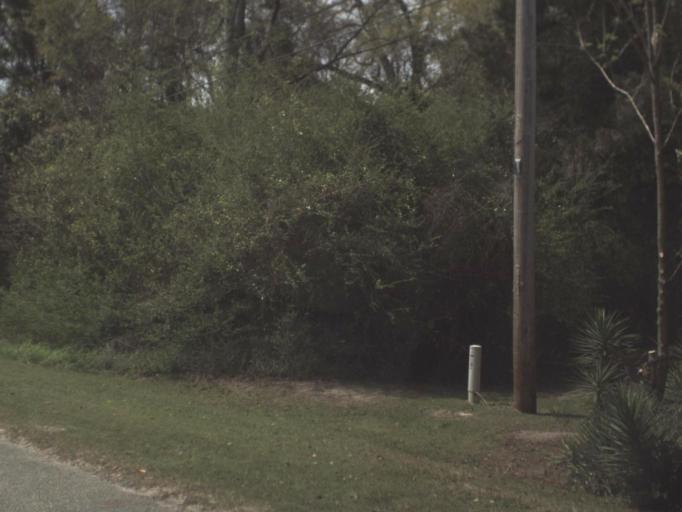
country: US
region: Florida
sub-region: Jackson County
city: Graceville
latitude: 30.9391
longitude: -85.5170
